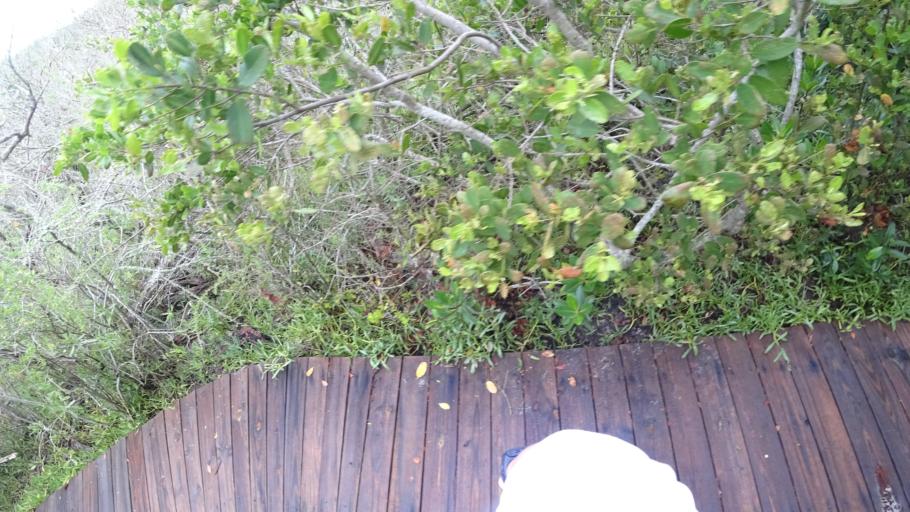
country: US
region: Florida
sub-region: Manatee County
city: Cortez
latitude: 27.4529
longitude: -82.6884
